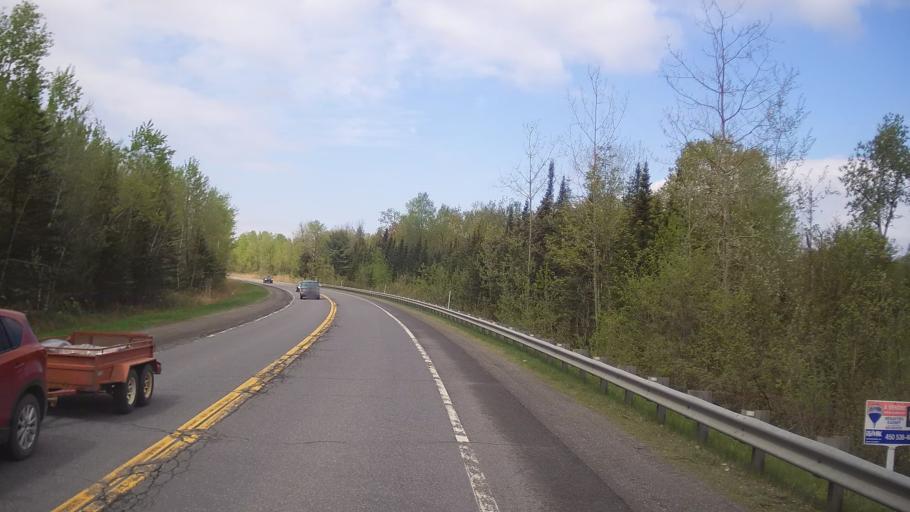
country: CA
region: Quebec
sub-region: Monteregie
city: Cowansville
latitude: 45.1979
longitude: -72.7276
